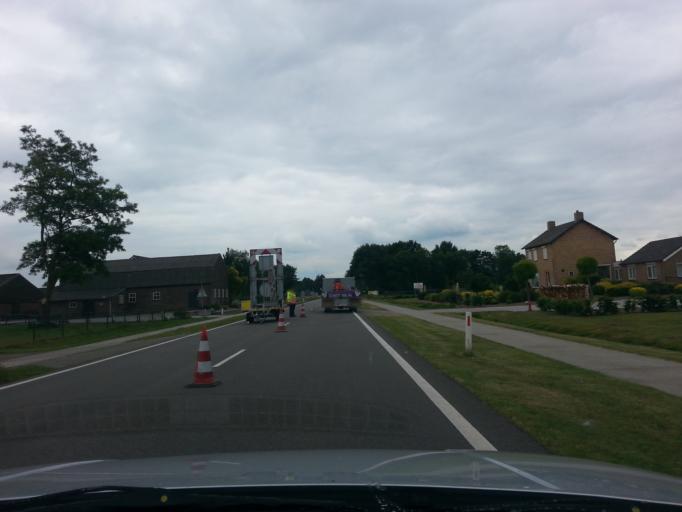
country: NL
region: Limburg
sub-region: Gemeente Venray
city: Venray
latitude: 51.5037
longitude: 5.8886
